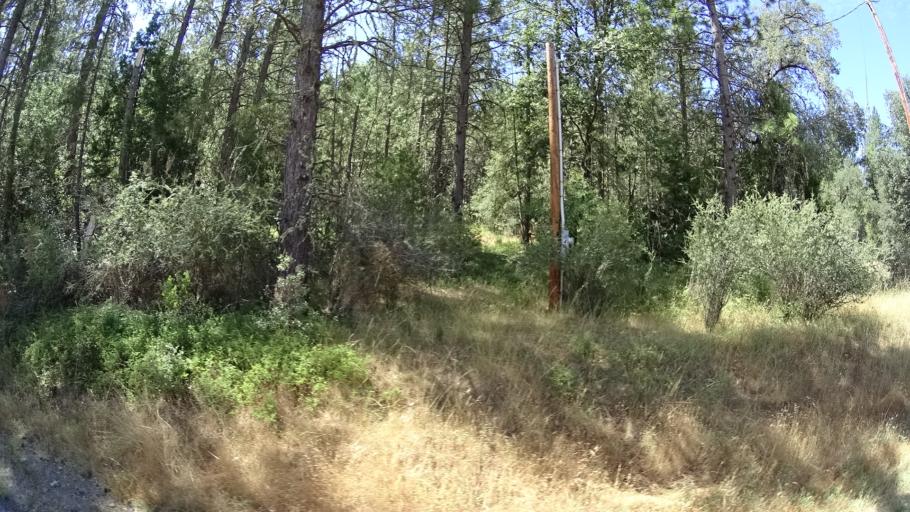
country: US
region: California
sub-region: Calaveras County
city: Mountain Ranch
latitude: 38.3373
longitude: -120.4985
